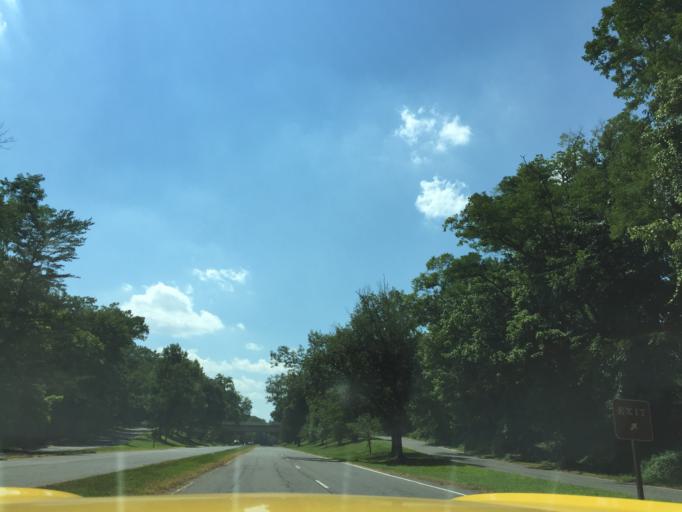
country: US
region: Maryland
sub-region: Montgomery County
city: Cabin John
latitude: 38.9712
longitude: -77.1499
